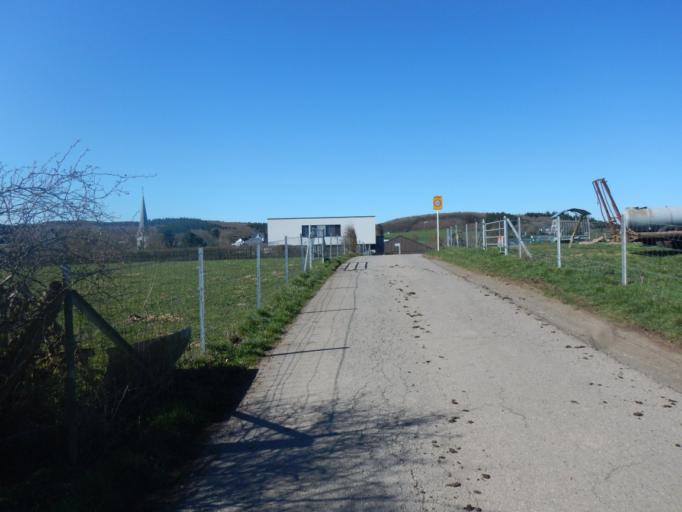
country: LU
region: Diekirch
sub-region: Canton de Wiltz
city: Eschweiler
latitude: 49.9956
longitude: 5.9511
